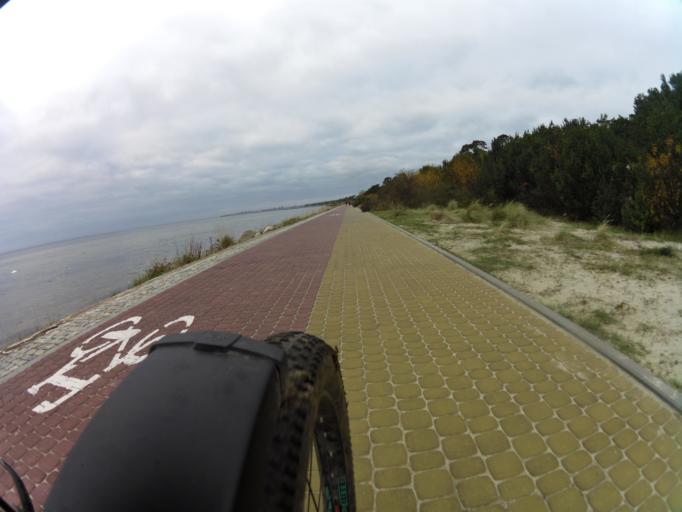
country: PL
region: Pomeranian Voivodeship
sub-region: Powiat pucki
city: Jastarnia
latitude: 54.6759
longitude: 18.7188
